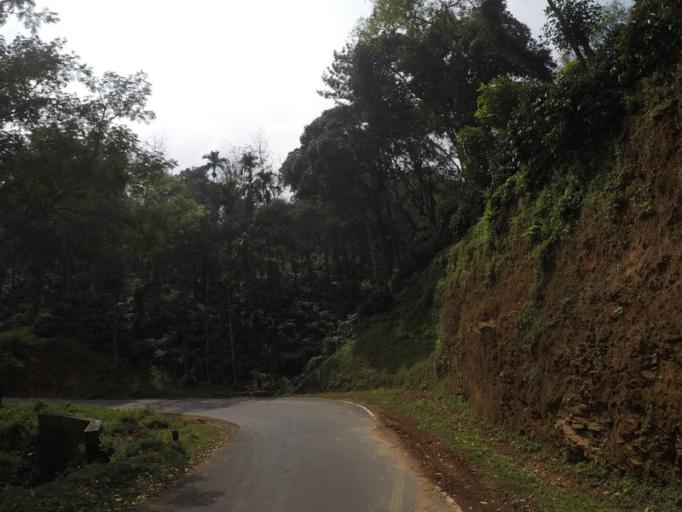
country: IN
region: Karnataka
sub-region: Chikmagalur
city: Mudigere
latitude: 13.1832
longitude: 75.4205
